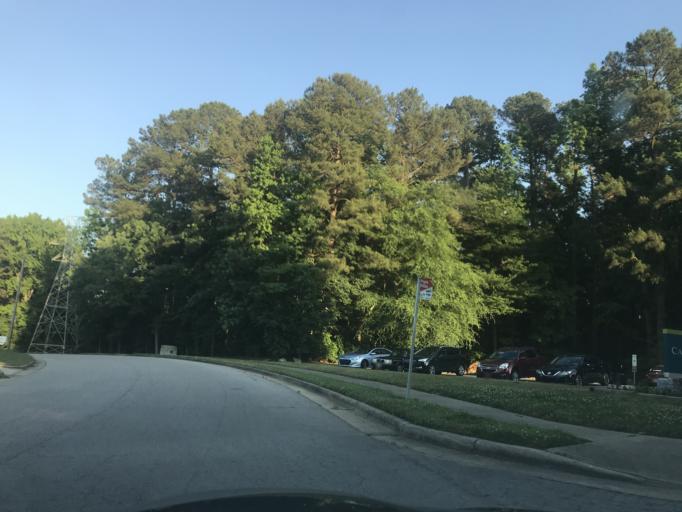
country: US
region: North Carolina
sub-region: Wake County
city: Raleigh
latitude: 35.7496
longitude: -78.6646
